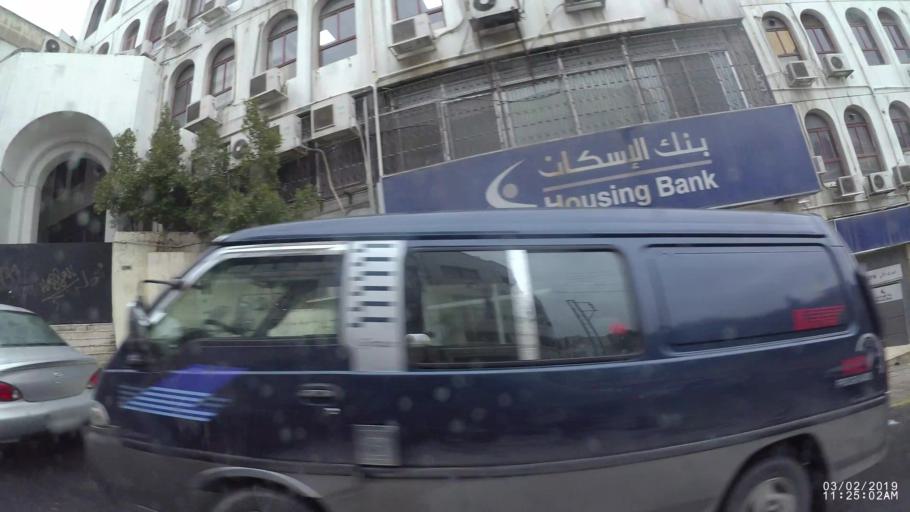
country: JO
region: Amman
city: Amman
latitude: 31.9515
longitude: 35.9276
